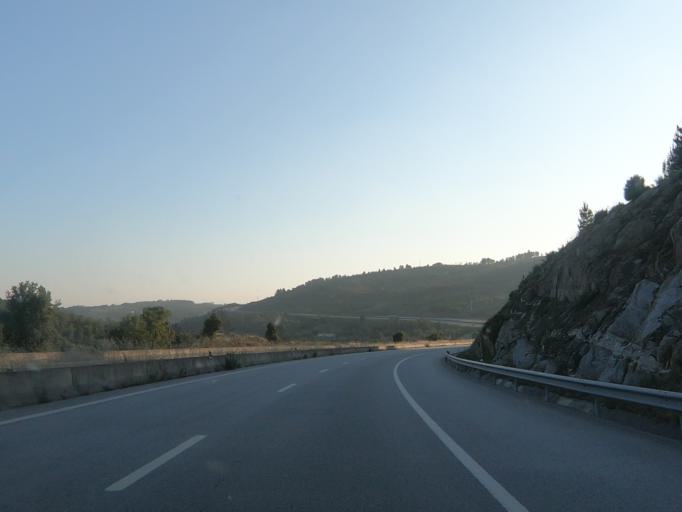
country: PT
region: Guarda
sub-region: Fornos de Algodres
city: Fornos de Algodres
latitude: 40.6307
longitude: -7.4697
